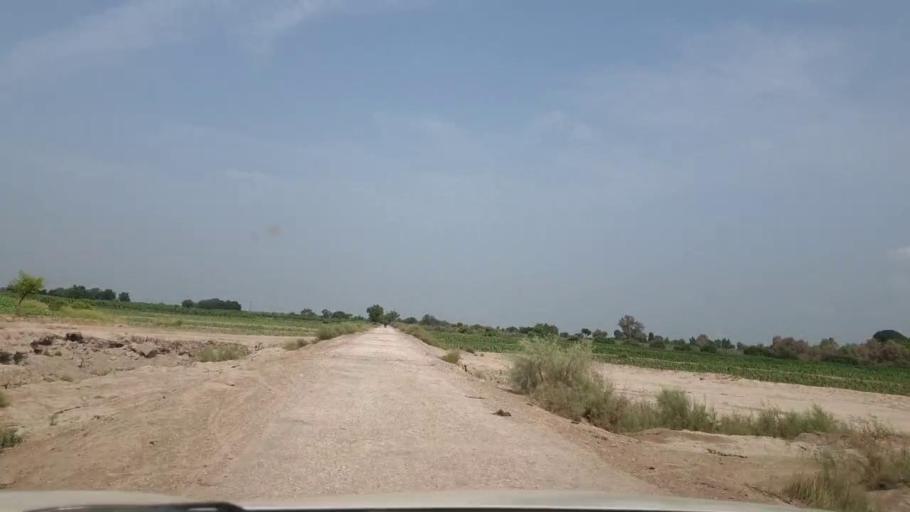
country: PK
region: Sindh
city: Sobhadero
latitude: 27.3882
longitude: 68.2733
